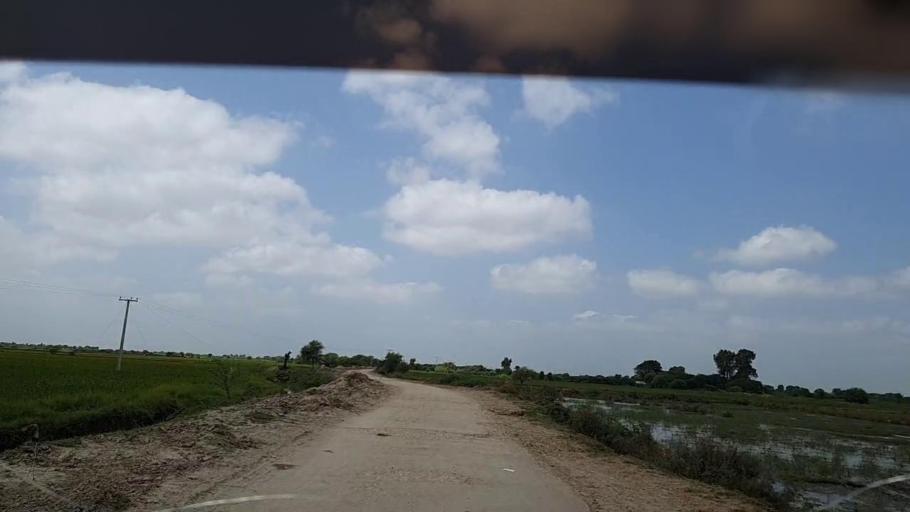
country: PK
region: Sindh
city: Badin
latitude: 24.5990
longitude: 68.7902
